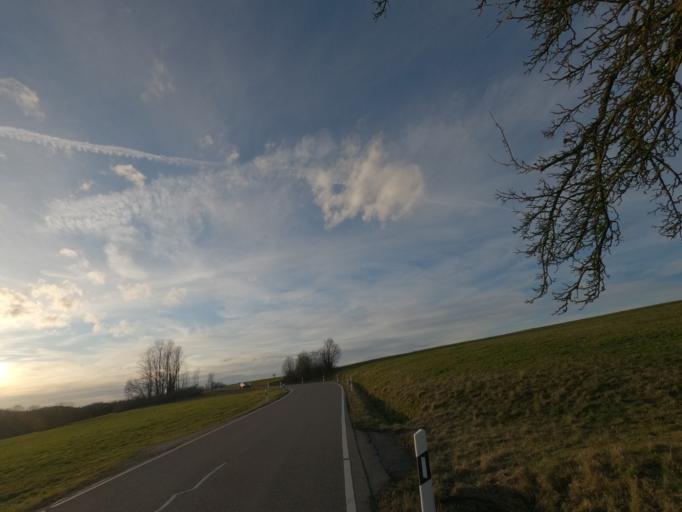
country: DE
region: Baden-Wuerttemberg
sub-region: Regierungsbezirk Stuttgart
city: Ottenbach
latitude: 48.7499
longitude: 9.7419
